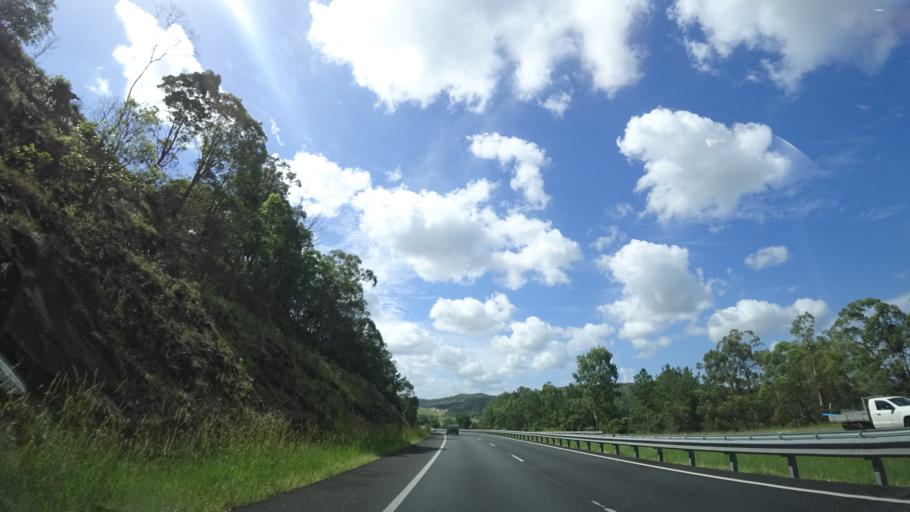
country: AU
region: Queensland
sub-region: Sunshine Coast
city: Twin Waters
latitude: -26.6247
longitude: 152.9878
